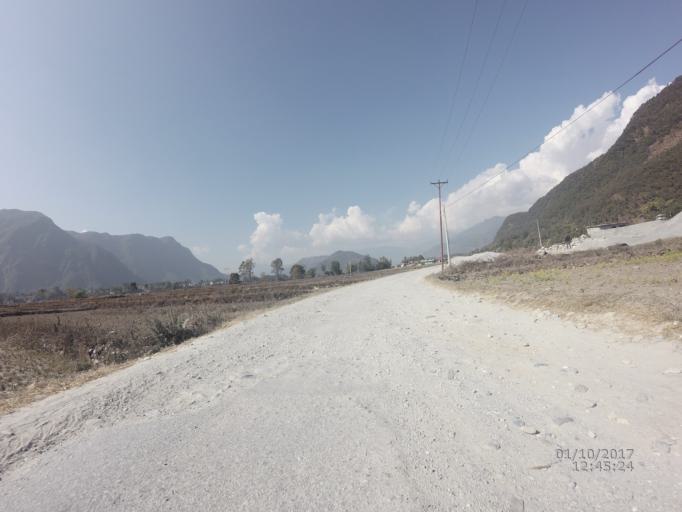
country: NP
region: Western Region
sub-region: Gandaki Zone
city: Pokhara
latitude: 28.2700
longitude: 83.9601
